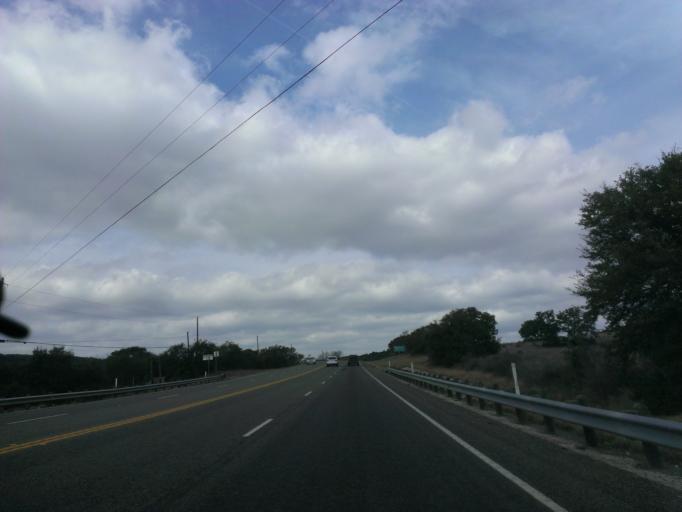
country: US
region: Texas
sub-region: Travis County
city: Briarcliff
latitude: 30.4299
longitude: -98.1388
